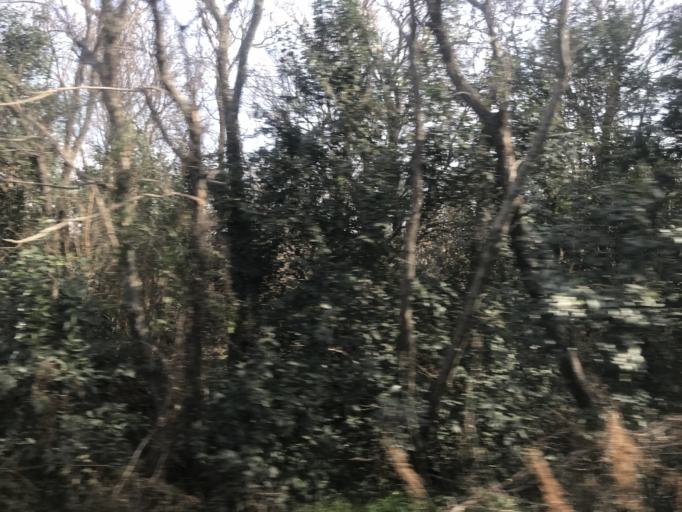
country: AR
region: Cordoba
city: Laguna Larga
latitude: -31.8069
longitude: -63.7768
